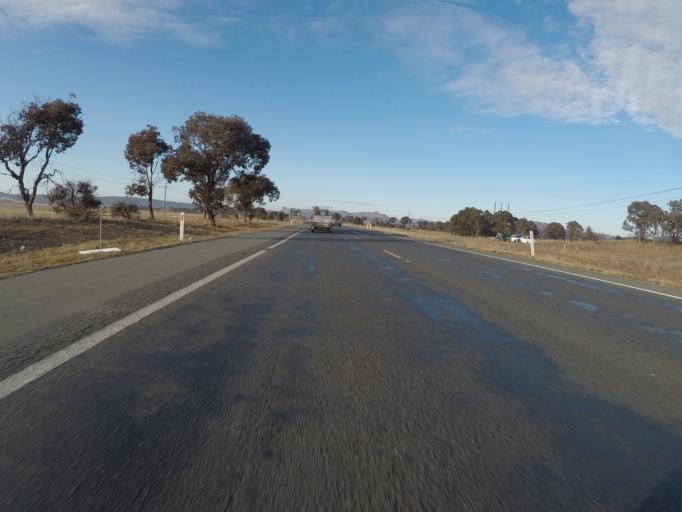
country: AU
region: Australian Capital Territory
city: Forrest
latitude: -35.3485
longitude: 149.1638
